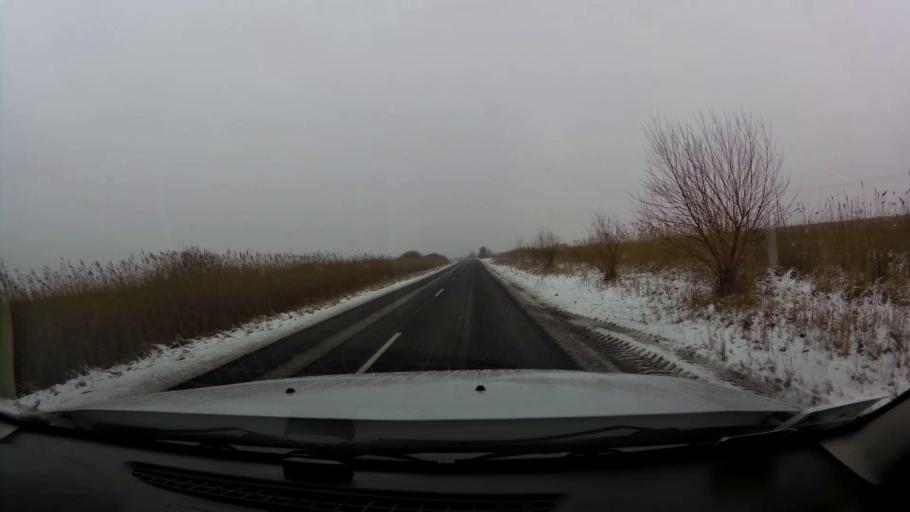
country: PL
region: West Pomeranian Voivodeship
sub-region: Powiat gryficki
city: Mrzezyno
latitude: 54.1191
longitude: 15.2685
